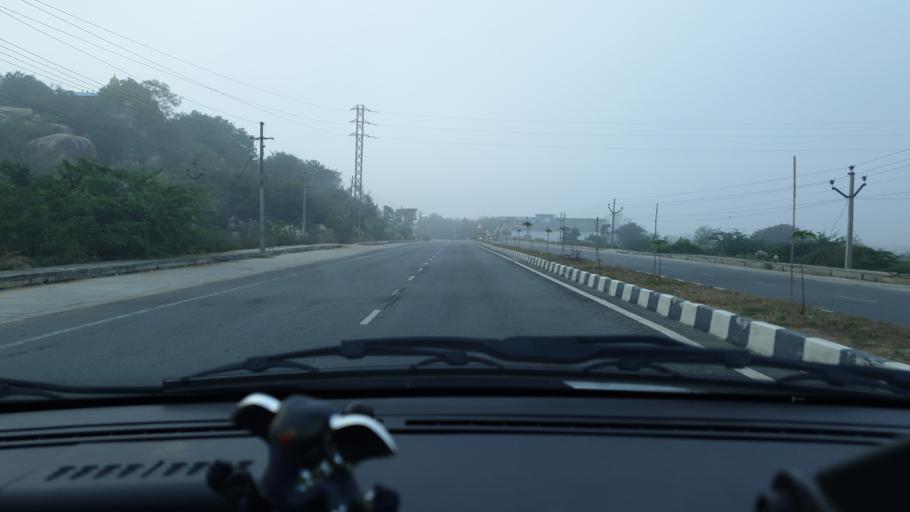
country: IN
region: Telangana
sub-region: Mahbubnagar
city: Farrukhnagar
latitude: 16.8628
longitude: 78.5285
